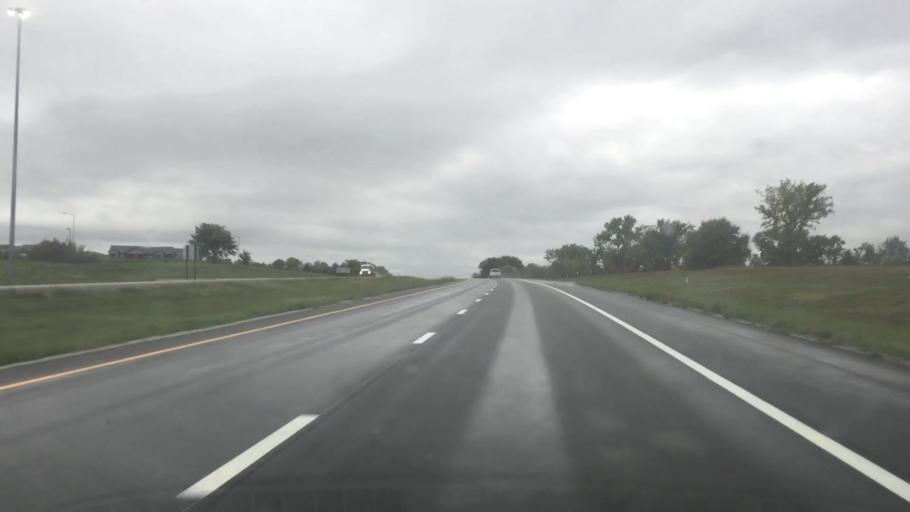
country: US
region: Kansas
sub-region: Johnson County
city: Spring Hill
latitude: 38.7224
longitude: -94.8346
